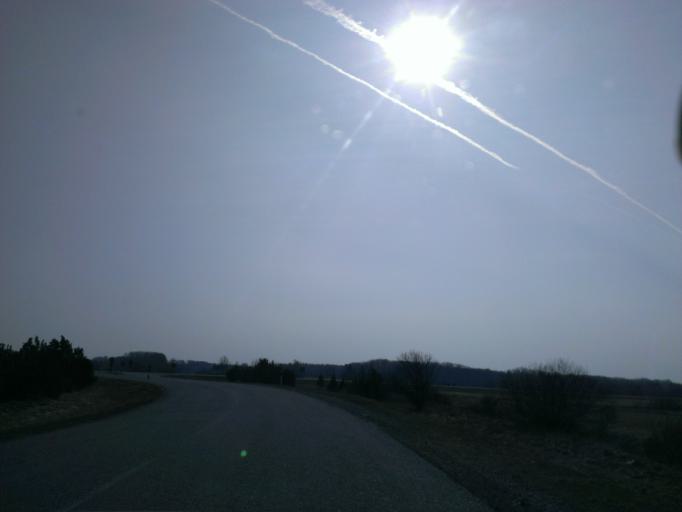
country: EE
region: Saare
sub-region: Orissaare vald
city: Orissaare
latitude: 58.5389
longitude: 23.1107
